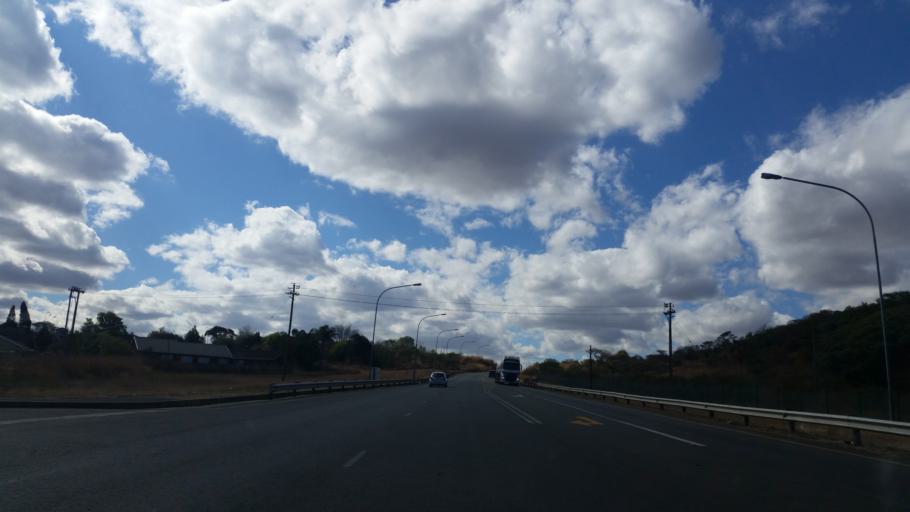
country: ZA
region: KwaZulu-Natal
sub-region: uThukela District Municipality
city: Ladysmith
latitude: -28.5319
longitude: 29.8062
